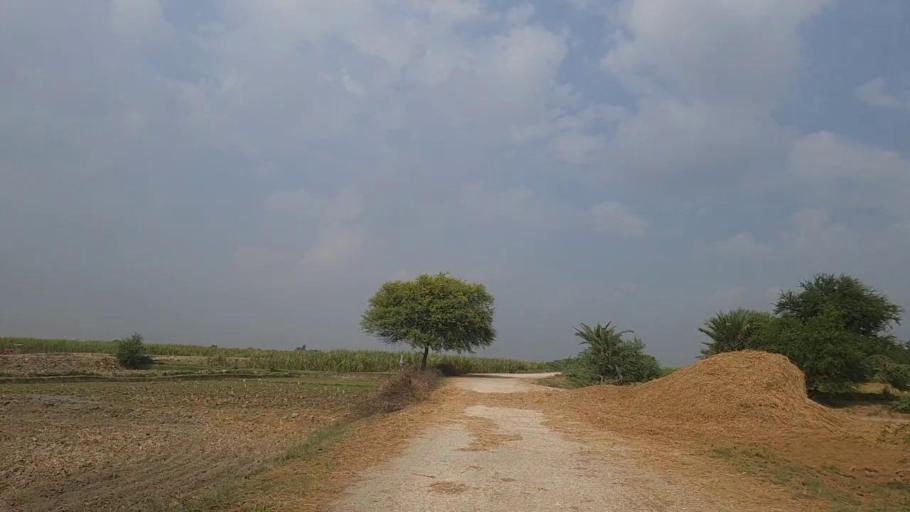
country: PK
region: Sindh
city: Daro Mehar
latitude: 24.6917
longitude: 68.1264
